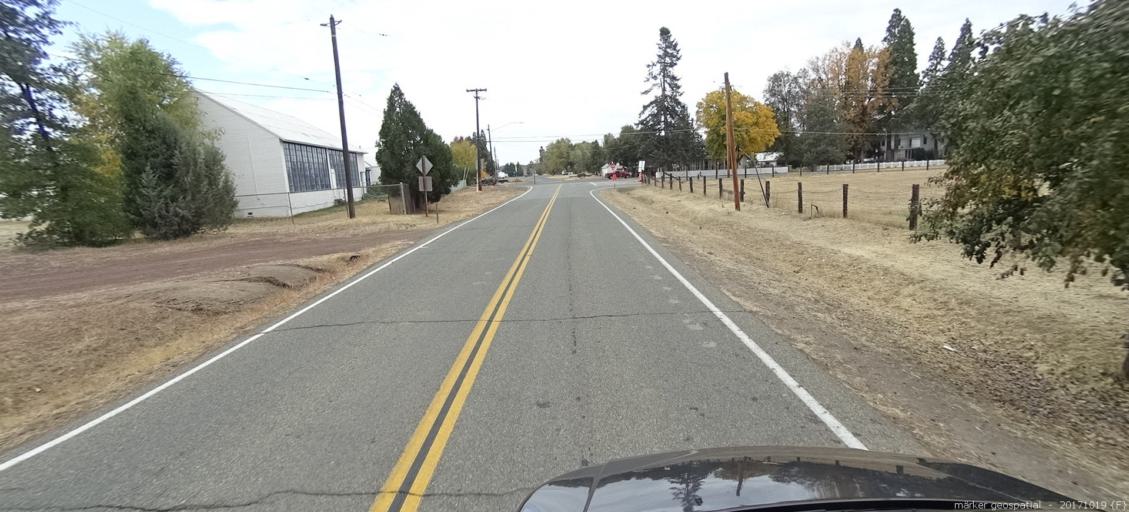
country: US
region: California
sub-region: Shasta County
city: Burney
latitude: 41.0483
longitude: -121.3972
